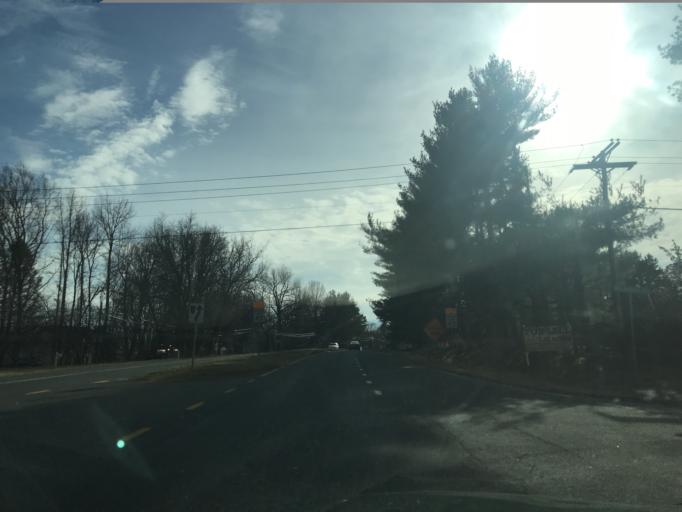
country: US
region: Maryland
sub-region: Prince George's County
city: Woodmore
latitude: 38.9429
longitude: -76.7989
